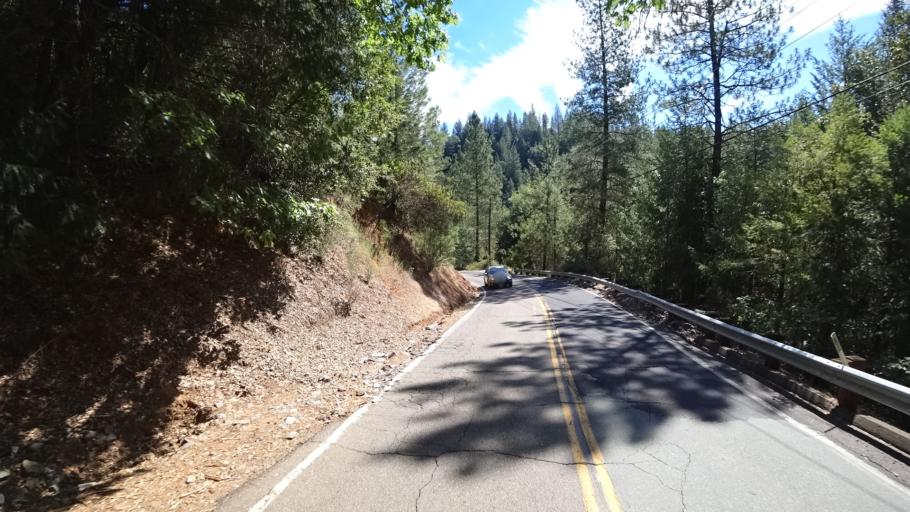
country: US
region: California
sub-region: Amador County
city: Pioneer
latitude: 38.3565
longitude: -120.5047
